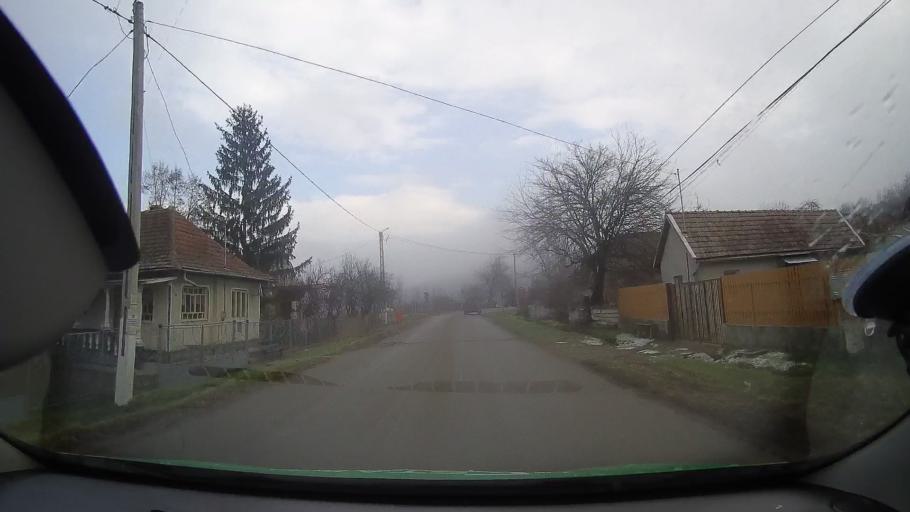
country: RO
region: Alba
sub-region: Comuna Noslac
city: Noslac
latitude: 46.4089
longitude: 23.9431
